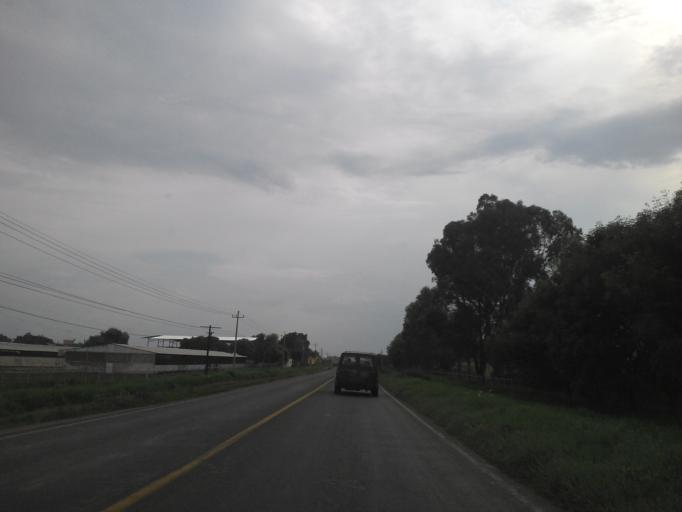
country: MX
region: Jalisco
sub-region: Acatic
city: Tierras Coloradas
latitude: 20.7557
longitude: -102.8267
